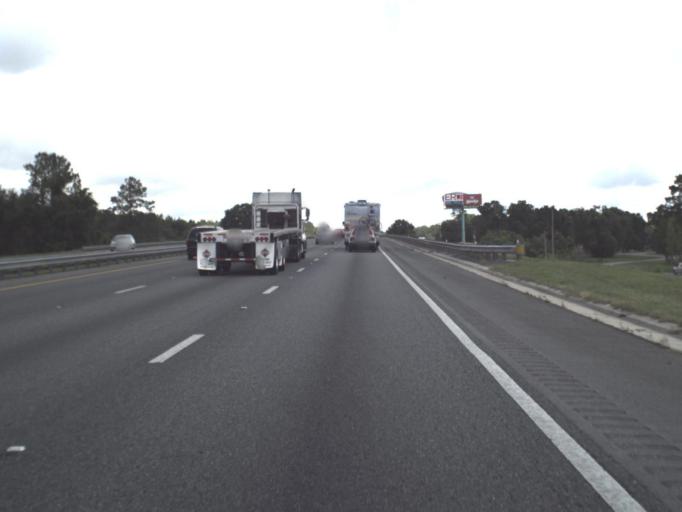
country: US
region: Florida
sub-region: Columbia County
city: Lake City
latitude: 30.1438
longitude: -82.6700
